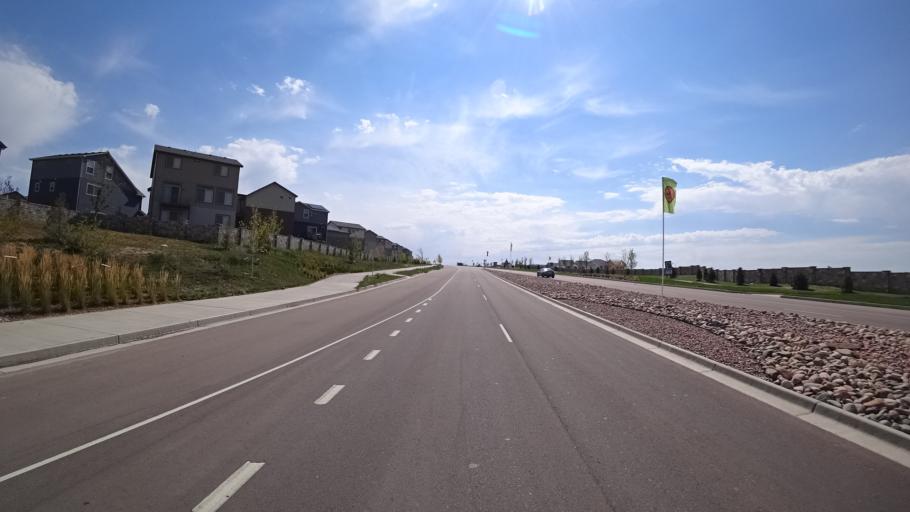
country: US
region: Colorado
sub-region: El Paso County
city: Cimarron Hills
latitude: 38.9268
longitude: -104.6625
